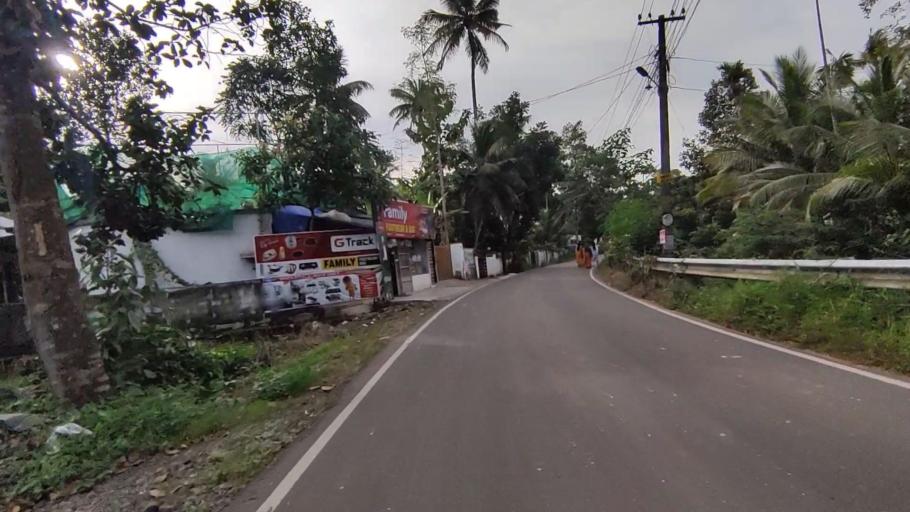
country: IN
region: Kerala
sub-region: Kottayam
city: Kottayam
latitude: 9.6030
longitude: 76.4917
